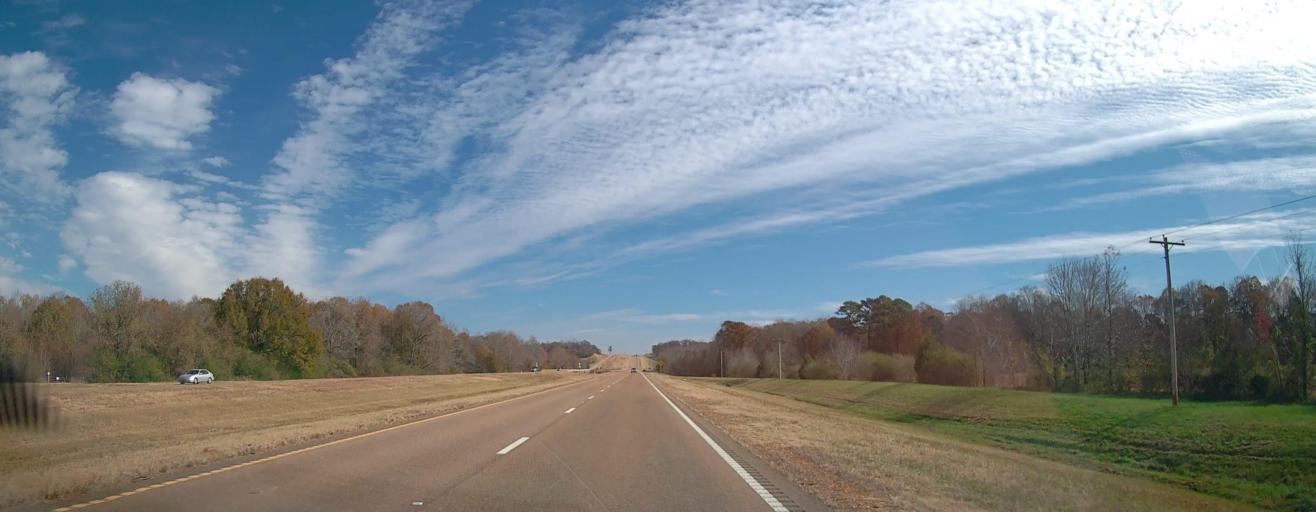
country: US
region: Mississippi
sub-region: Benton County
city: Ashland
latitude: 34.9460
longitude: -89.2015
